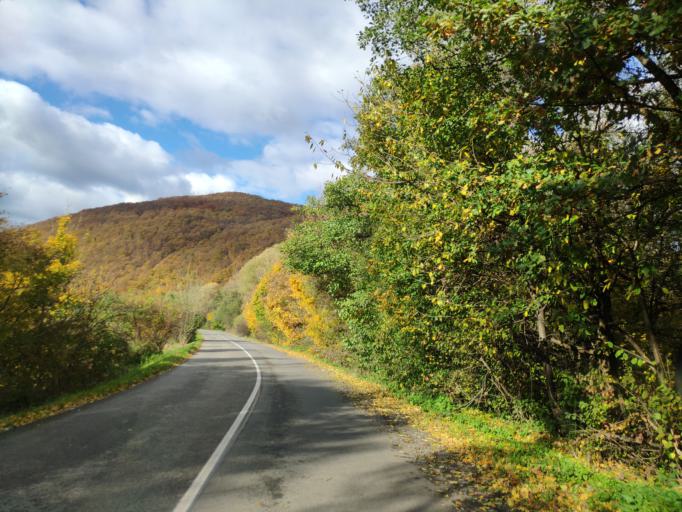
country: SK
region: Presovsky
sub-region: Okres Presov
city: Presov
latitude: 48.8592
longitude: 21.2268
